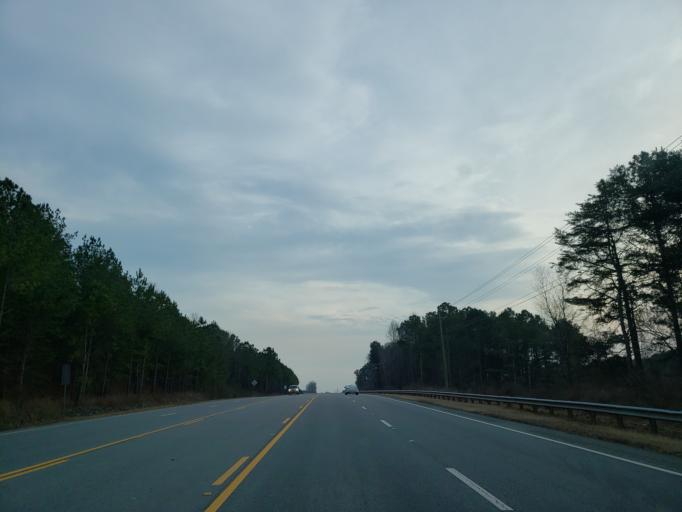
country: US
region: Georgia
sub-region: Whitfield County
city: Varnell
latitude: 34.9650
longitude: -84.9367
